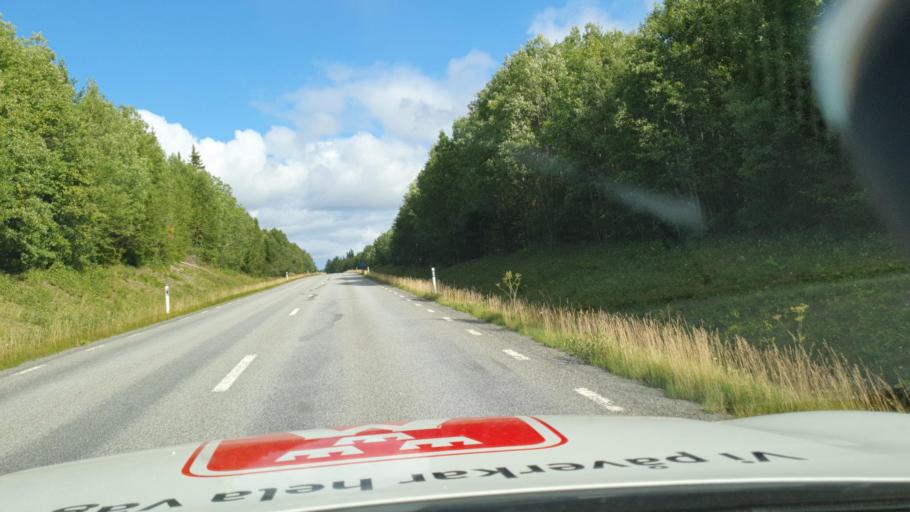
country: SE
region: Jaemtland
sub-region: OEstersunds Kommun
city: Lit
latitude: 63.4562
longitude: 15.1722
